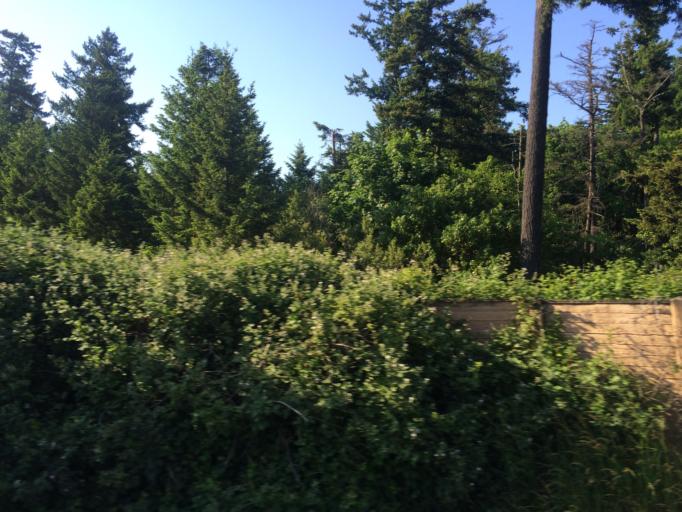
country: CA
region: British Columbia
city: Colwood
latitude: 48.4633
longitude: -123.4368
